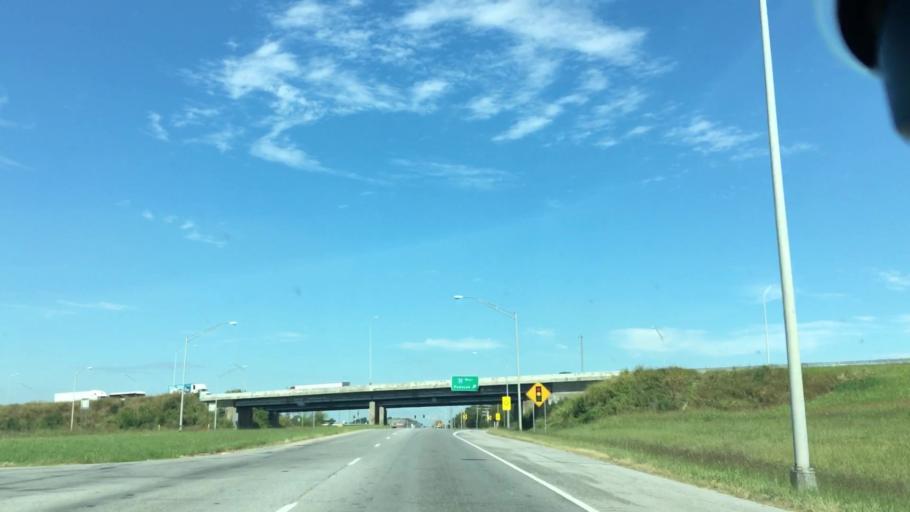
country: US
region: Kentucky
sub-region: Christian County
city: Oak Grove
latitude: 36.7012
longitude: -87.4545
